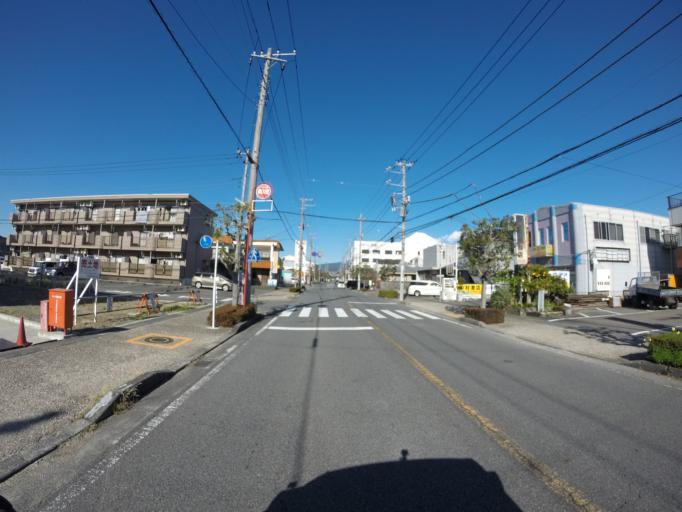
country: JP
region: Shizuoka
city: Fuji
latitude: 35.1647
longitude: 138.6535
